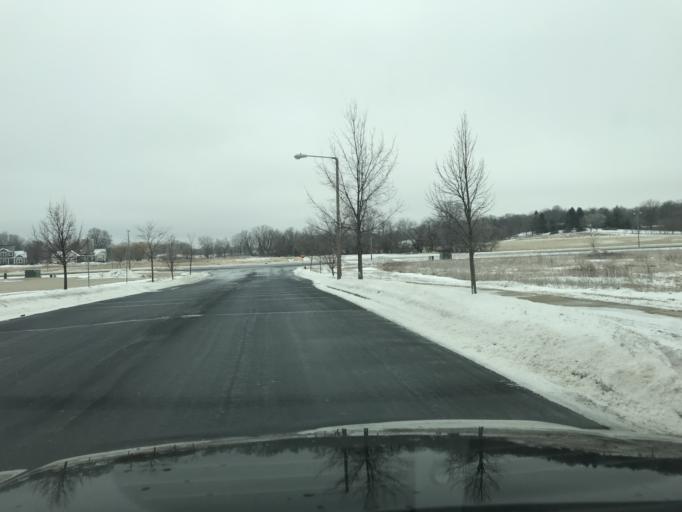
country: US
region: Wisconsin
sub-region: Dane County
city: Cottage Grove
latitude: 43.0893
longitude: -89.2154
